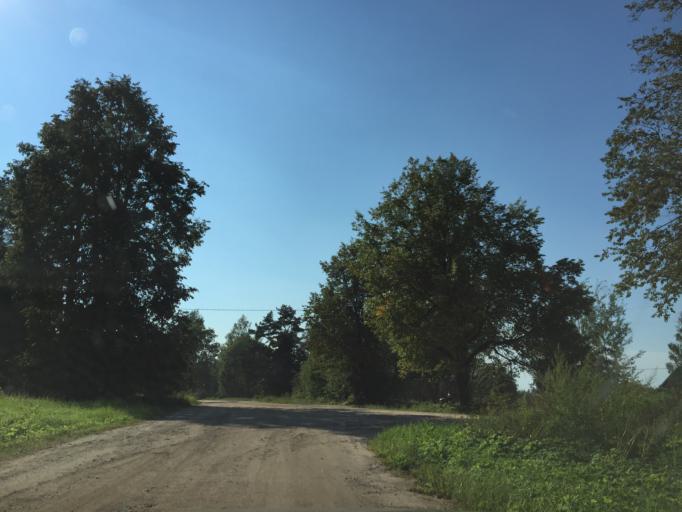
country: LV
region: Limbazu Rajons
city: Limbazi
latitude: 57.5487
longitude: 24.7661
